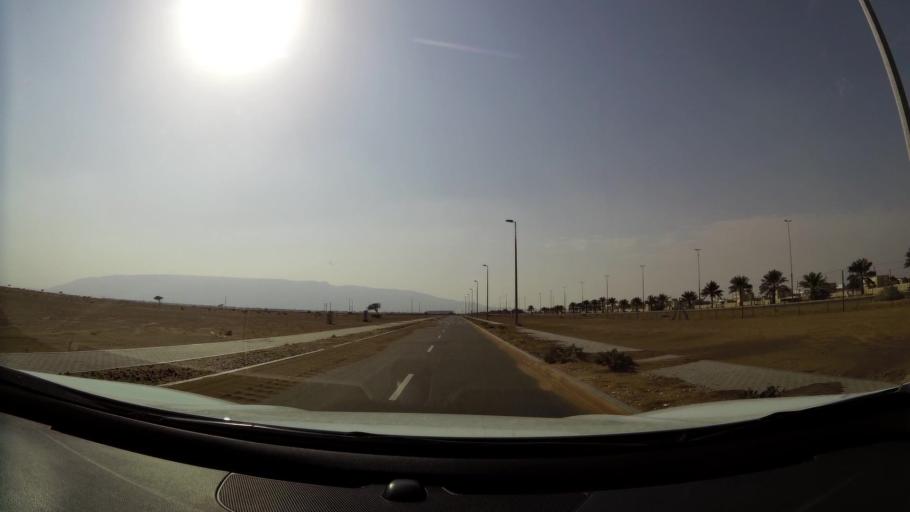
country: AE
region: Abu Dhabi
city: Al Ain
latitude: 24.0925
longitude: 55.8952
